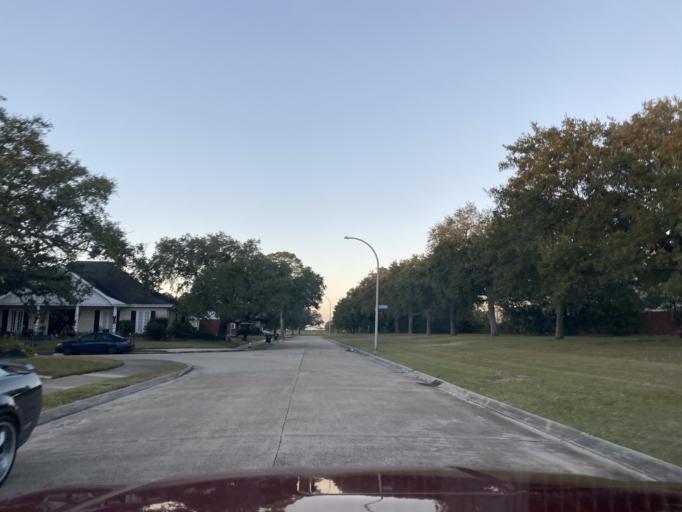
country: US
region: Louisiana
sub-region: Orleans Parish
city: New Orleans
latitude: 30.0279
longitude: -90.0551
